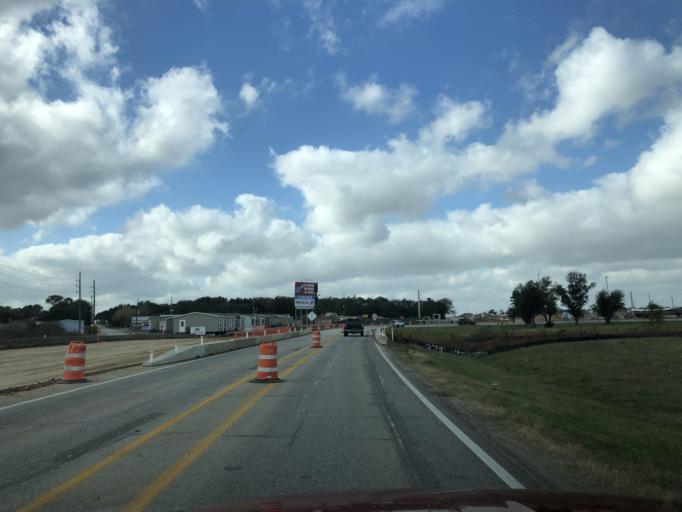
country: US
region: Texas
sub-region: Austin County
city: Sealy
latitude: 29.7626
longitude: -96.1555
